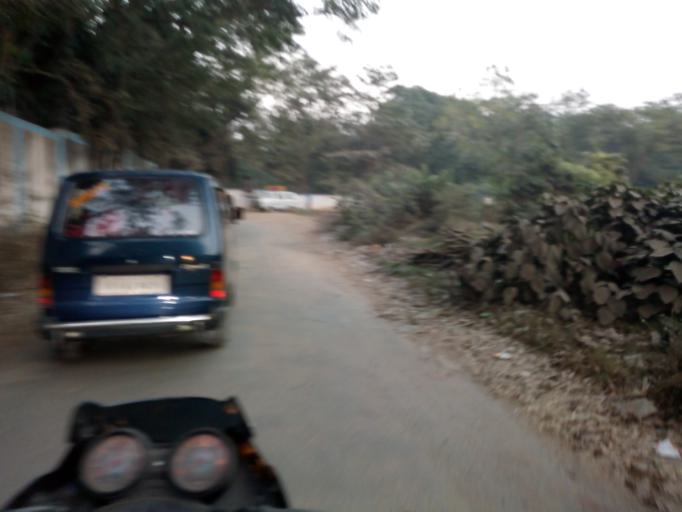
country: IN
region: West Bengal
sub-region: Bankura
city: Bankura
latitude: 23.2379
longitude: 87.0318
